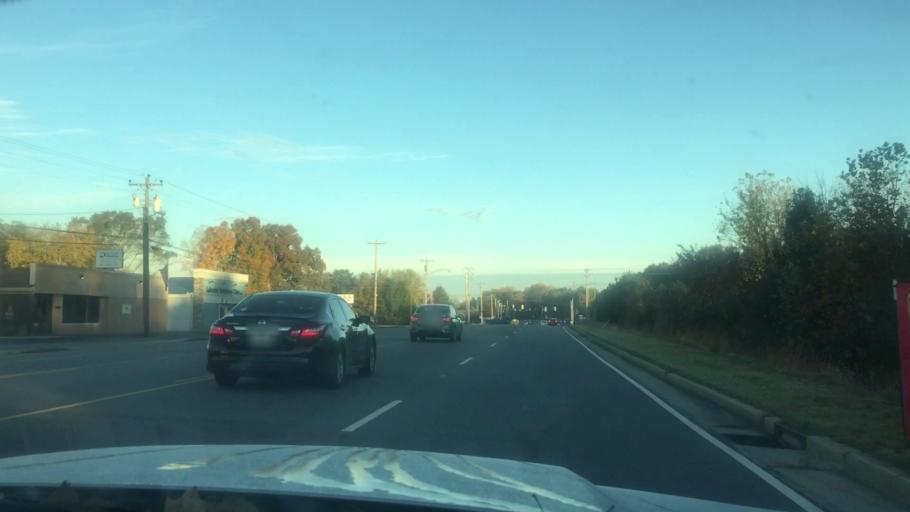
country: US
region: Tennessee
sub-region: Franklin County
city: Estill Springs
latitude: 35.2688
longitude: -86.1267
